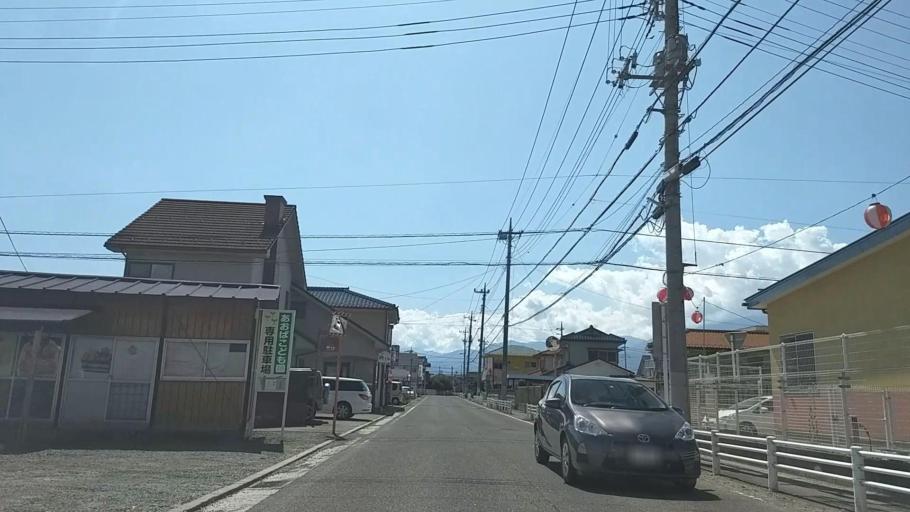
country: JP
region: Yamanashi
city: Ryuo
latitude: 35.6558
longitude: 138.5205
